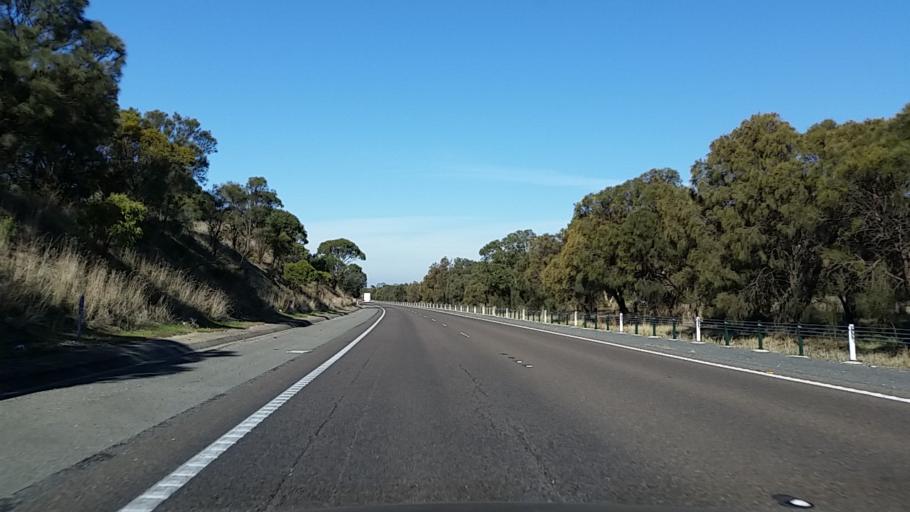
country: AU
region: South Australia
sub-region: Mount Barker
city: Nairne
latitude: -35.0804
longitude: 138.9525
